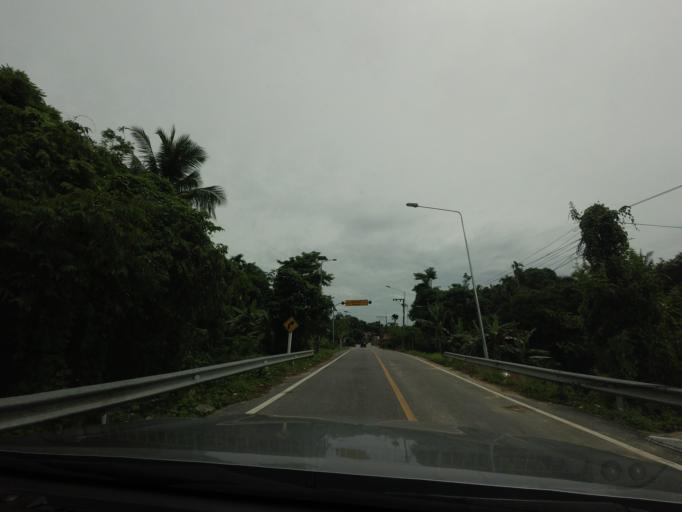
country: TH
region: Pattani
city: Kapho
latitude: 6.5922
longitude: 101.5312
